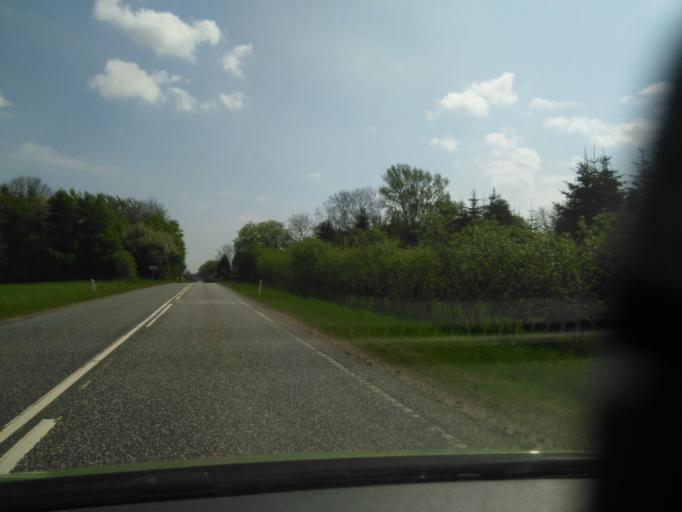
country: DK
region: Central Jutland
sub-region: Arhus Kommune
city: Solbjerg
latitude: 55.9817
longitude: 10.0468
